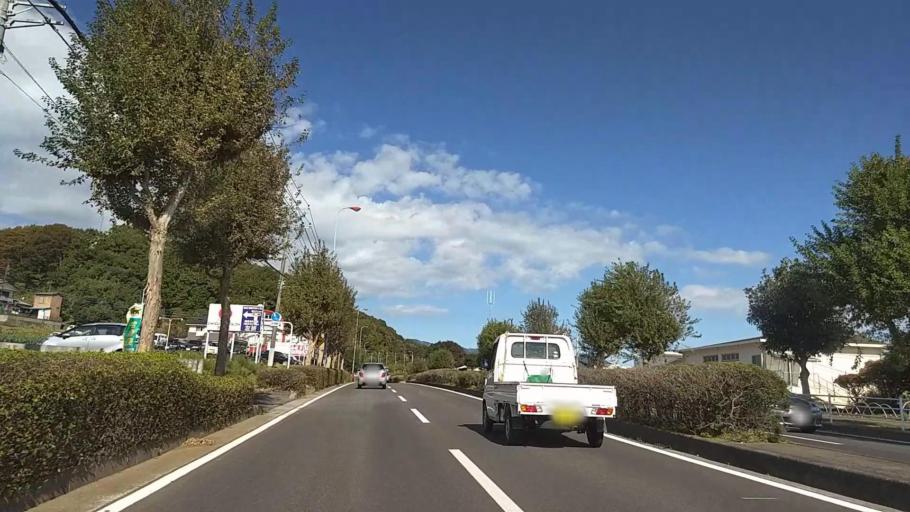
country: JP
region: Kanagawa
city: Hadano
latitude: 35.3403
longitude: 139.2301
